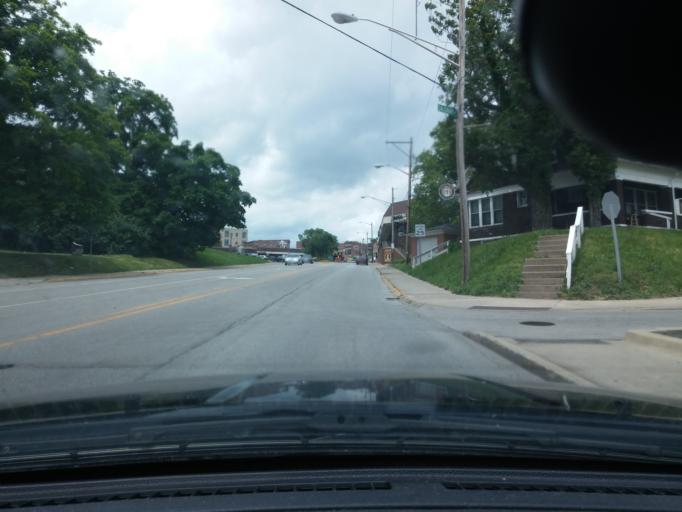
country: US
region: Indiana
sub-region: Tippecanoe County
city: West Lafayette
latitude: 40.4227
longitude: -86.9056
